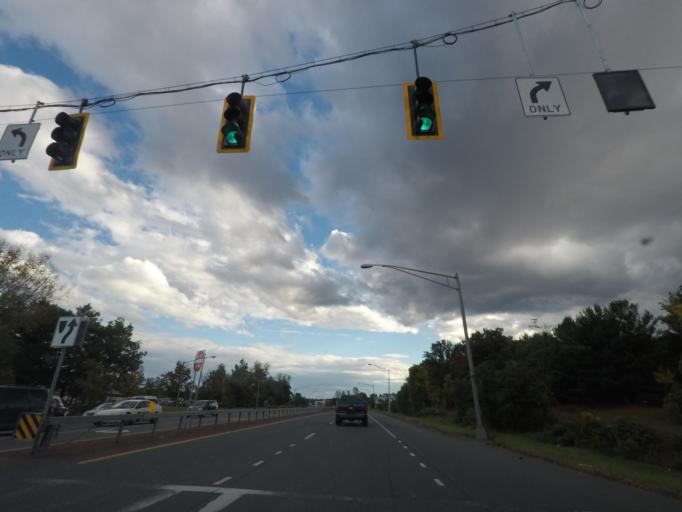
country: US
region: New York
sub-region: Albany County
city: McKownville
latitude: 42.6960
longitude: -73.8498
